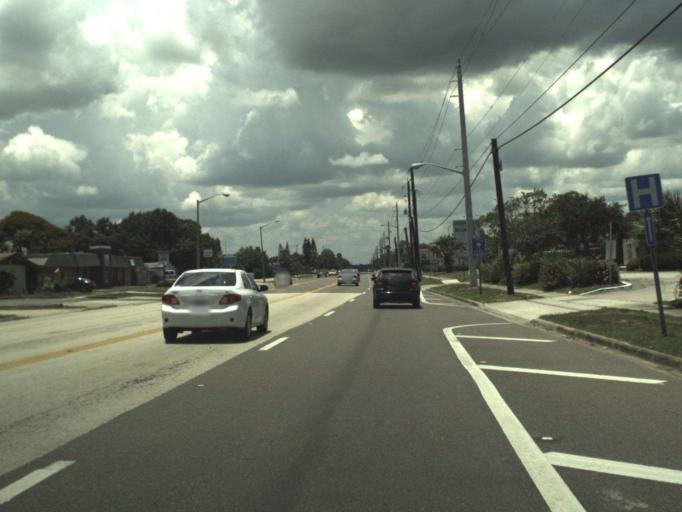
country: US
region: Florida
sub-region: Brevard County
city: West Melbourne
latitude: 28.1217
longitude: -80.6551
